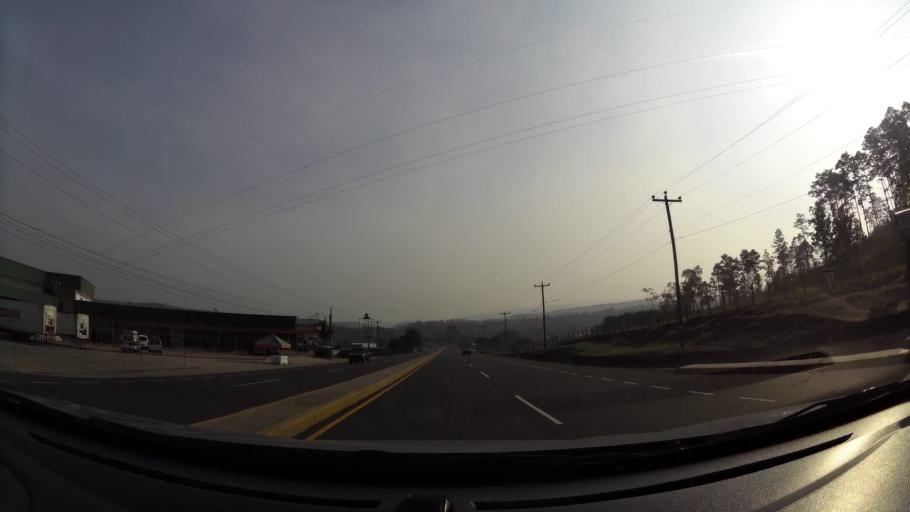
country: HN
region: Francisco Morazan
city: Zambrano
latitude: 14.2769
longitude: -87.4051
